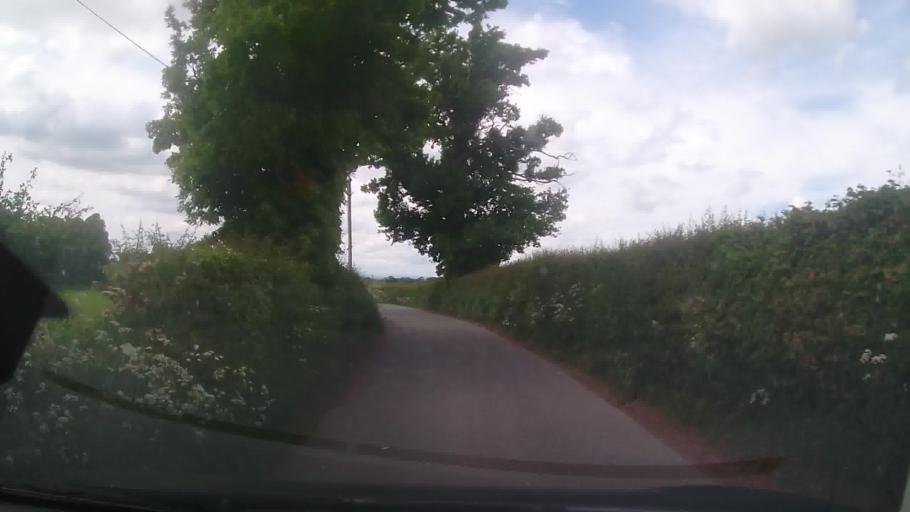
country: GB
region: England
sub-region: Shropshire
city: Clive
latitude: 52.8071
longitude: -2.7279
